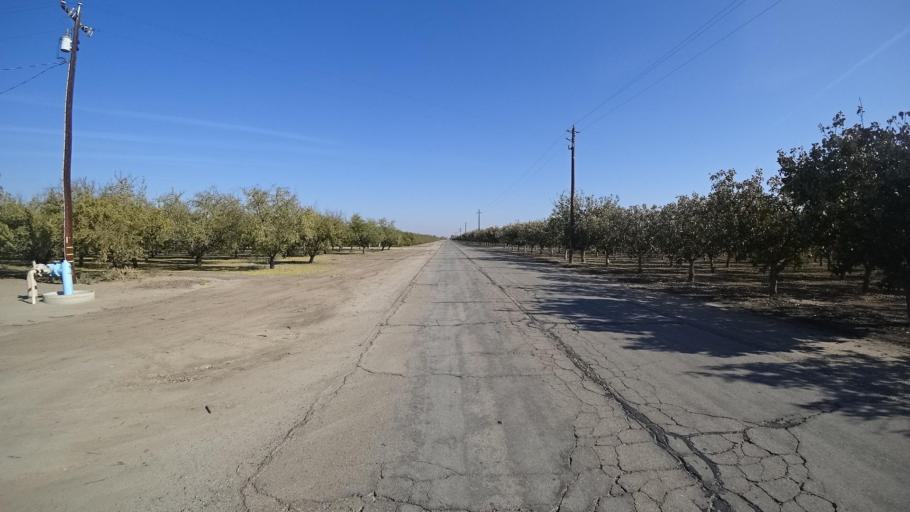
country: US
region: California
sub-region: Kern County
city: Wasco
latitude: 35.6669
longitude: -119.3582
